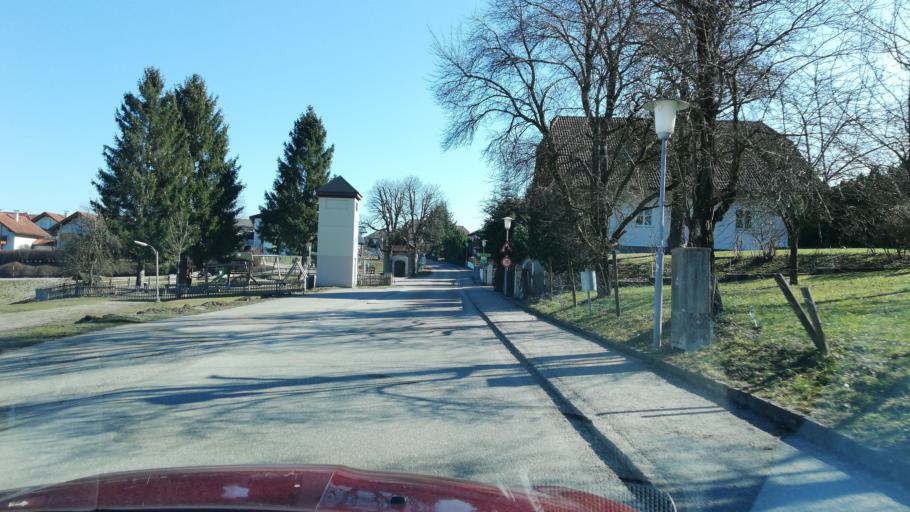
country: AT
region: Upper Austria
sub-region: Politischer Bezirk Vocklabruck
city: Aurach am Hongar
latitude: 47.9518
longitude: 13.6739
